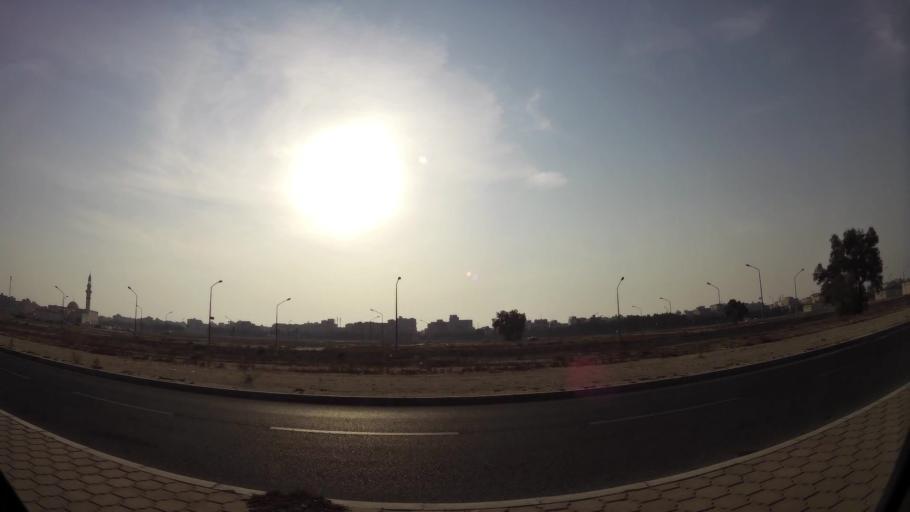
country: KW
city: Al Funaytis
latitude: 29.2392
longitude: 48.0871
